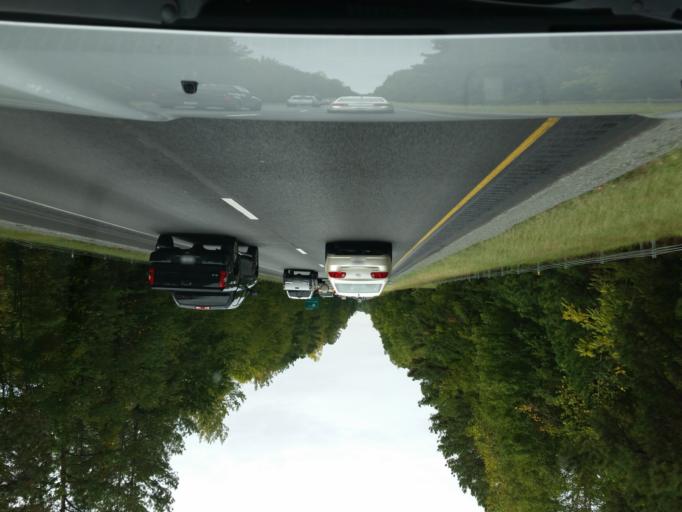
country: US
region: Virginia
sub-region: New Kent County
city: New Kent
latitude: 37.4844
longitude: -76.9475
